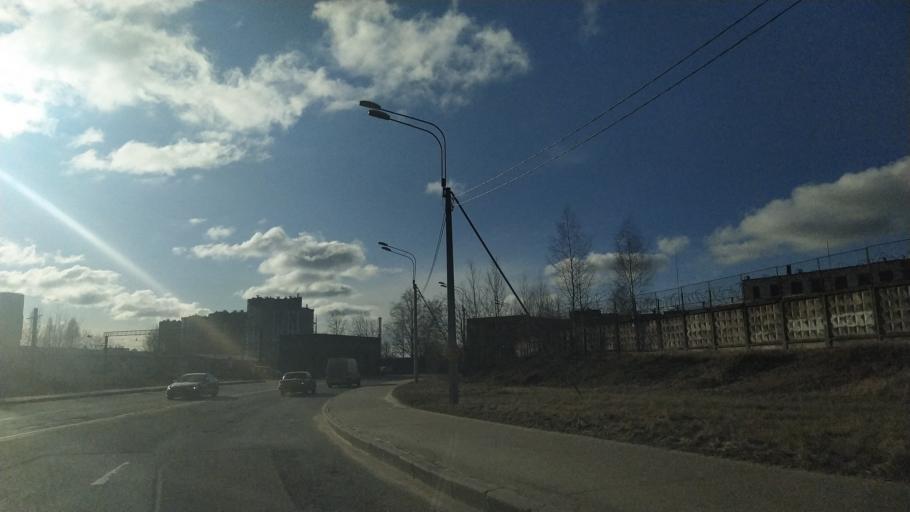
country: RU
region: St.-Petersburg
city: Kushelevka
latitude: 59.9922
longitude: 30.3757
